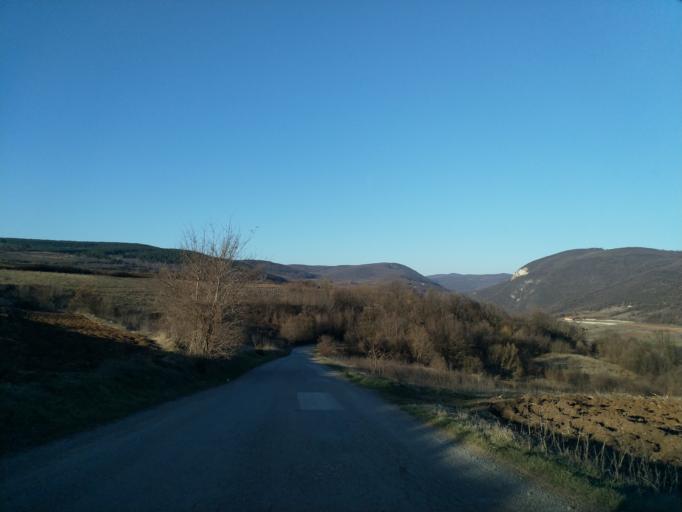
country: RS
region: Central Serbia
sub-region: Pomoravski Okrug
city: Paracin
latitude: 43.9274
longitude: 21.5128
